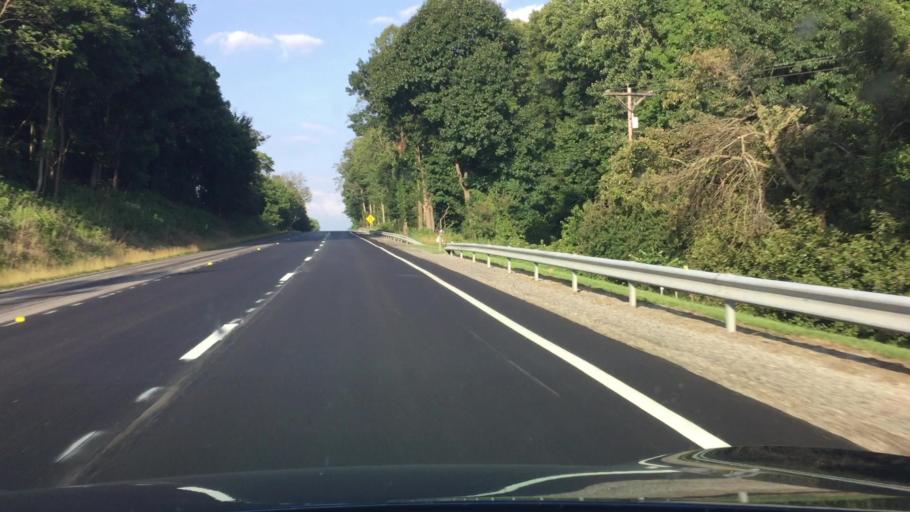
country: US
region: Virginia
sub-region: Montgomery County
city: Christiansburg
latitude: 37.1311
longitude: -80.4760
